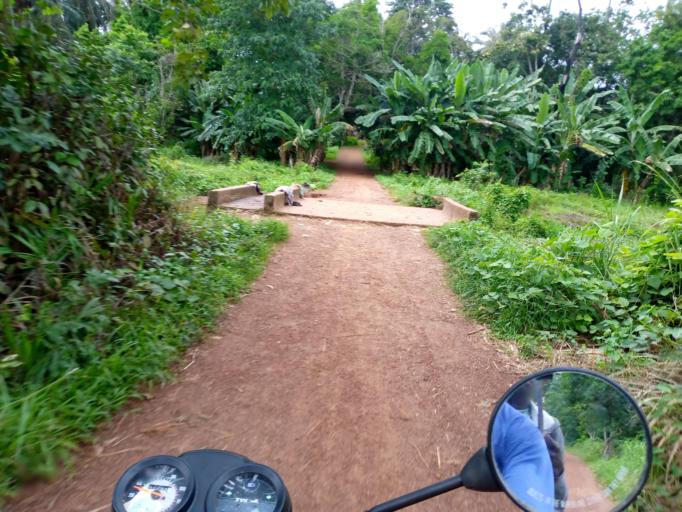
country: SL
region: Northern Province
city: Mange
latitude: 8.9781
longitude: -12.7097
